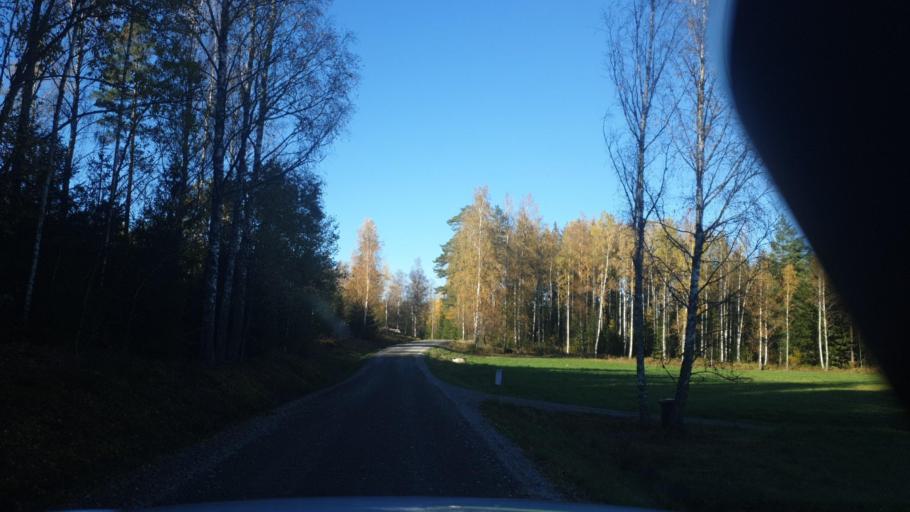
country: SE
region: Vaermland
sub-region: Arvika Kommun
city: Arvika
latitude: 59.5728
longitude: 12.8324
